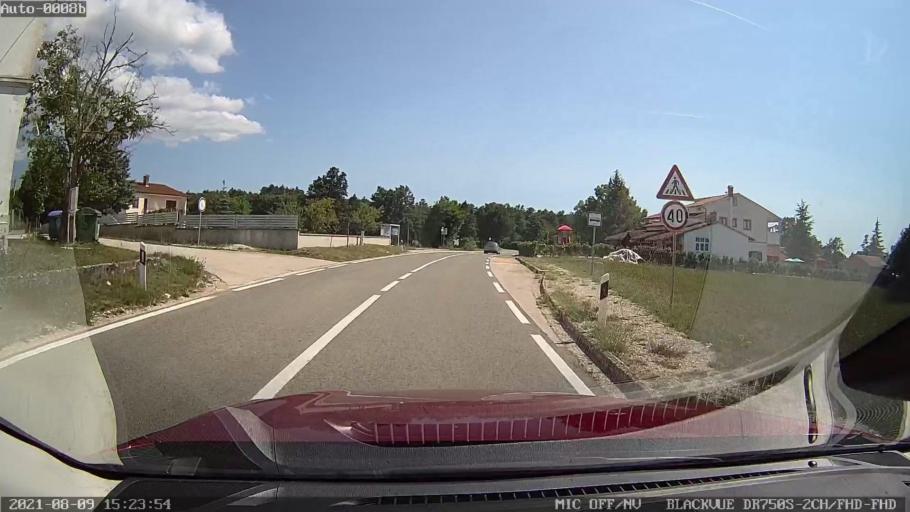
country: HR
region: Istarska
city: Pazin
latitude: 45.1795
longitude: 13.9046
